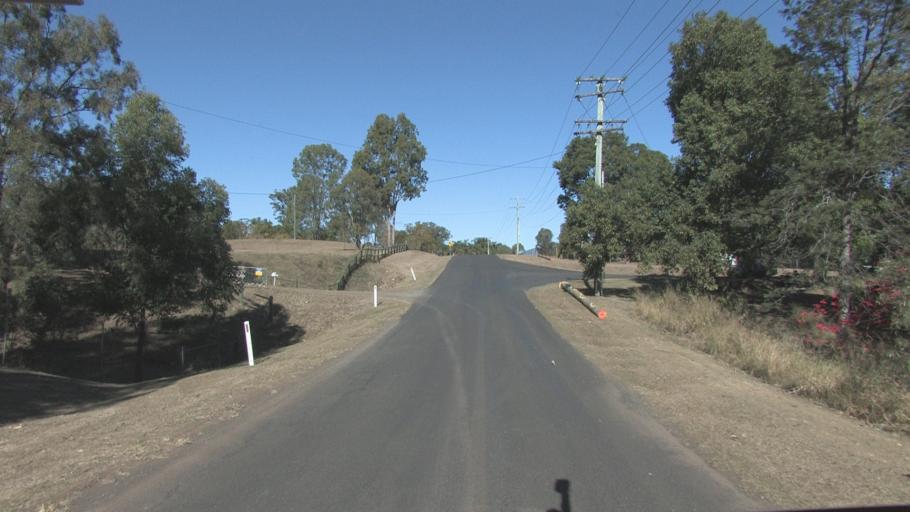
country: AU
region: Queensland
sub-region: Logan
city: Cedar Vale
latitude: -27.8902
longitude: 152.9775
